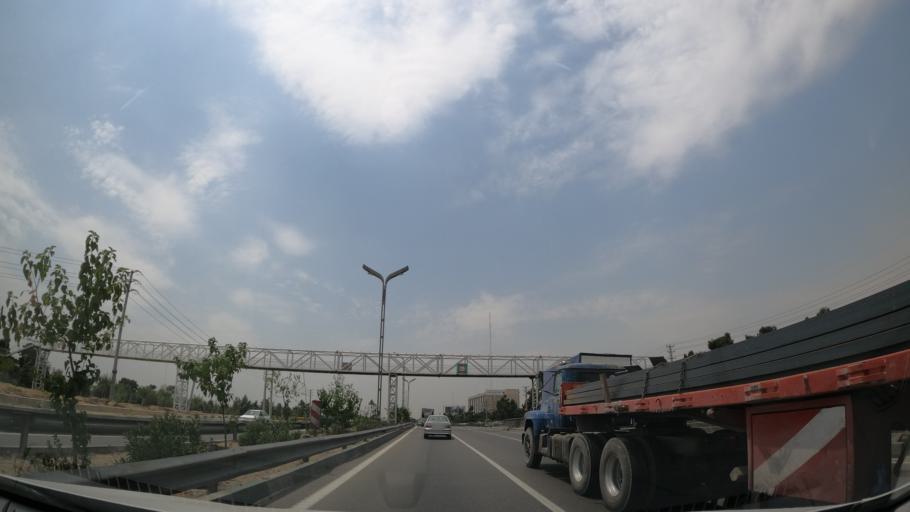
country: IR
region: Tehran
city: Shahr-e Qods
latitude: 35.7042
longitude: 51.1818
